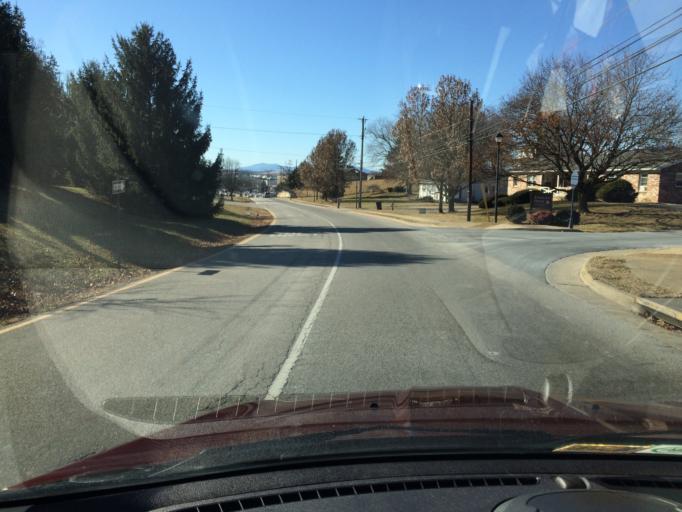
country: US
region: Virginia
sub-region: Rockingham County
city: Bridgewater
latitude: 38.3942
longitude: -78.9611
